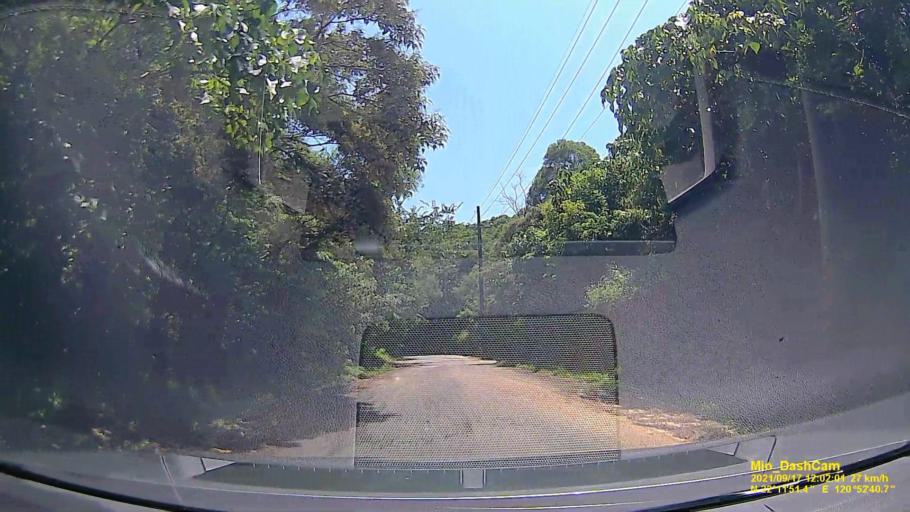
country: TW
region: Taiwan
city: Hengchun
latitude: 22.1976
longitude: 120.8780
